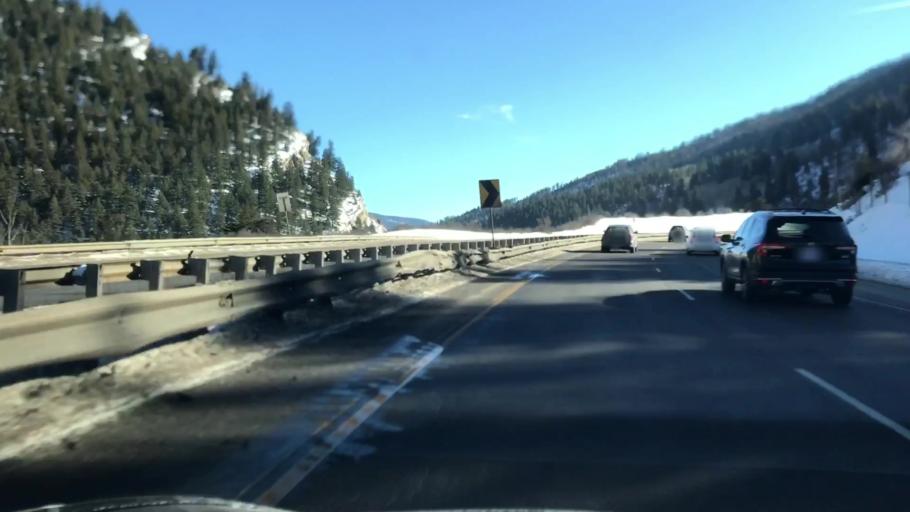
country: US
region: Colorado
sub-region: Eagle County
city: Minturn
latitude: 39.6152
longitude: -106.4597
